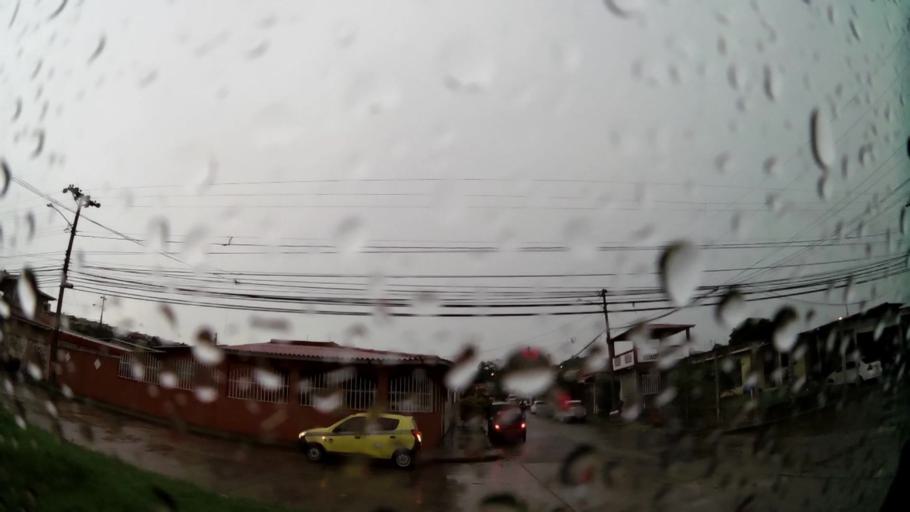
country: PA
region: Panama
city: San Miguelito
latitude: 9.0570
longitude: -79.4740
